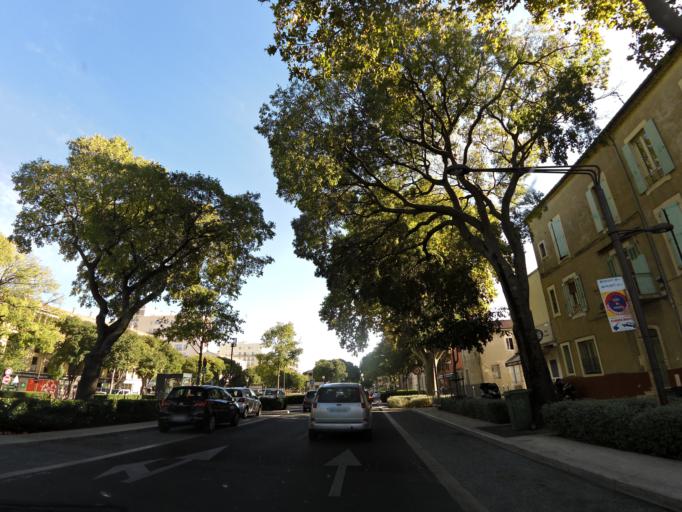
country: FR
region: Languedoc-Roussillon
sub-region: Departement du Gard
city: Nimes
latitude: 43.8337
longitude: 4.3512
